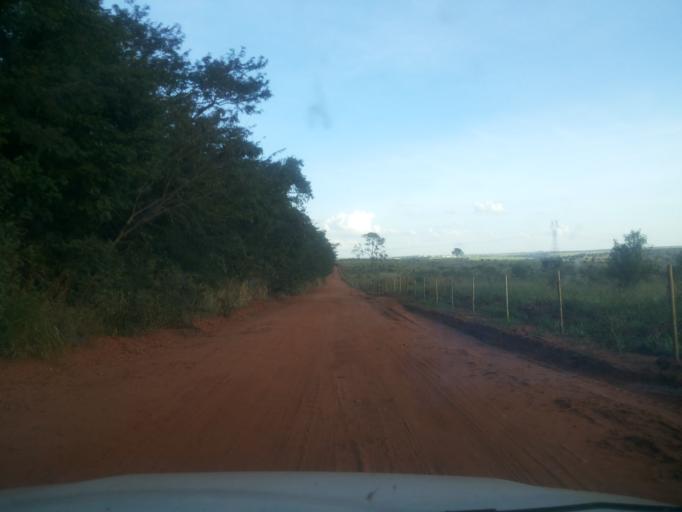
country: BR
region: Minas Gerais
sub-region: Santa Vitoria
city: Santa Vitoria
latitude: -19.0100
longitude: -50.3721
